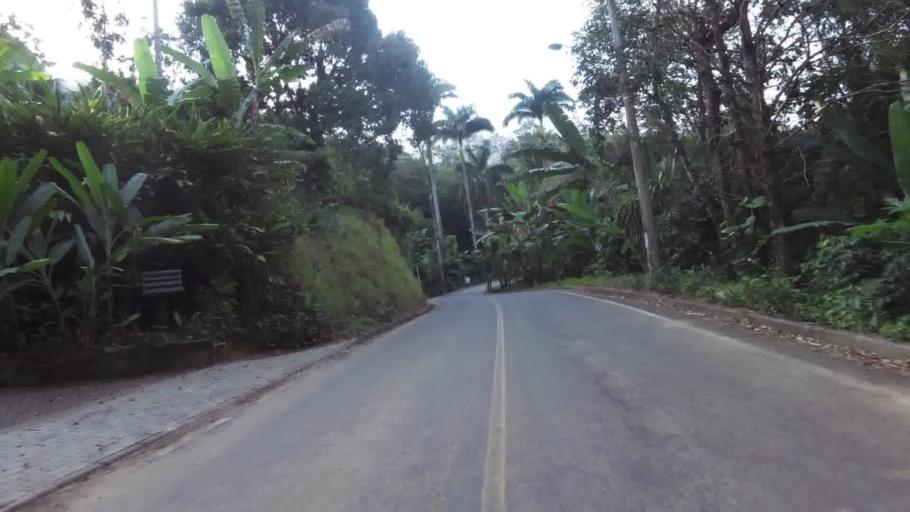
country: BR
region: Espirito Santo
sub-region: Alfredo Chaves
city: Alfredo Chaves
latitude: -20.5835
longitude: -40.6988
